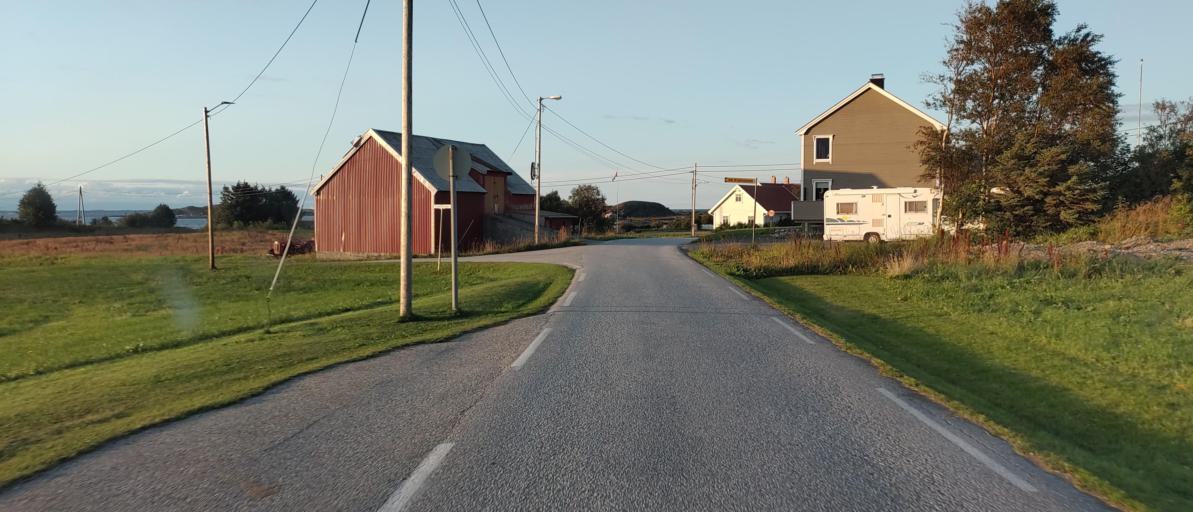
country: NO
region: More og Romsdal
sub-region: Fraena
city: Elnesvagen
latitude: 62.9971
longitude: 7.2236
